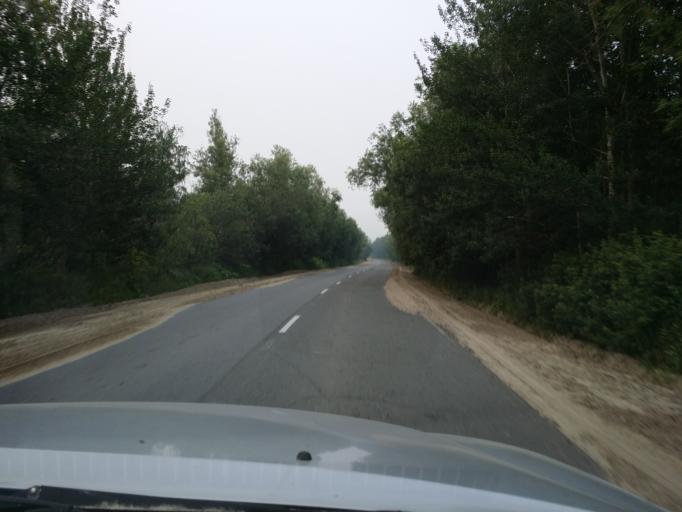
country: RU
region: Khanty-Mansiyskiy Avtonomnyy Okrug
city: Megion
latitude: 61.0025
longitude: 76.3065
